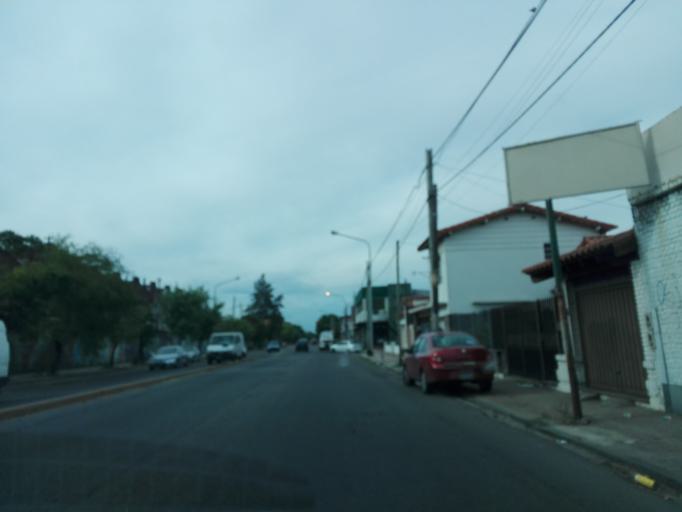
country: AR
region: Buenos Aires
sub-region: Partido de Lanus
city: Lanus
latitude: -34.7312
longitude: -58.3900
